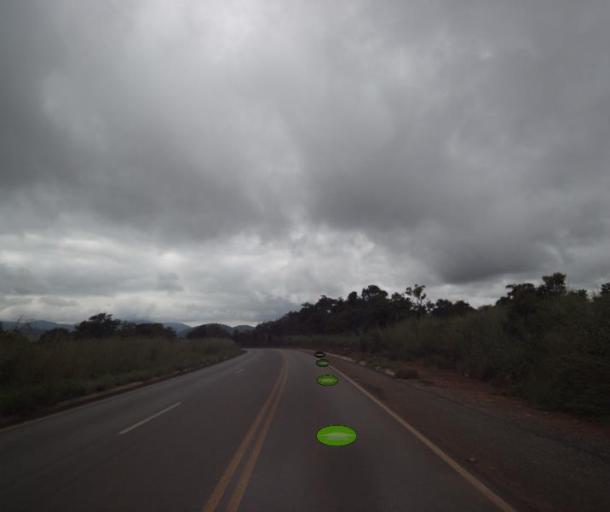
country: BR
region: Goias
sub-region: Barro Alto
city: Barro Alto
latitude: -14.8654
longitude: -49.0163
